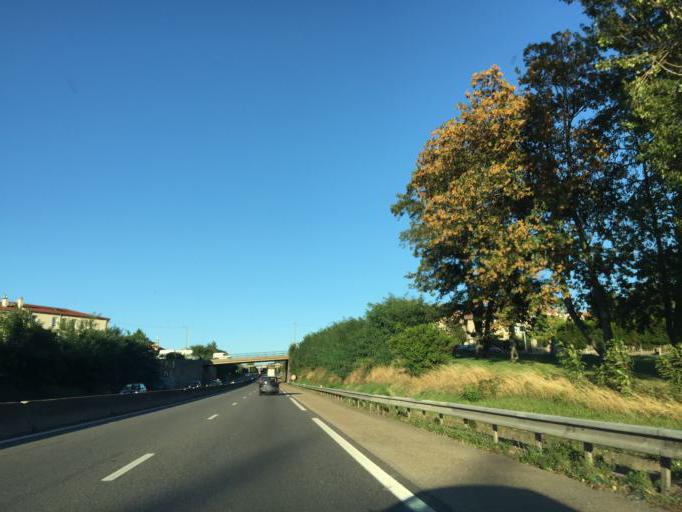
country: FR
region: Rhone-Alpes
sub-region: Departement de la Loire
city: Le Chambon-Feugerolles
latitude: 45.3942
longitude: 4.3293
